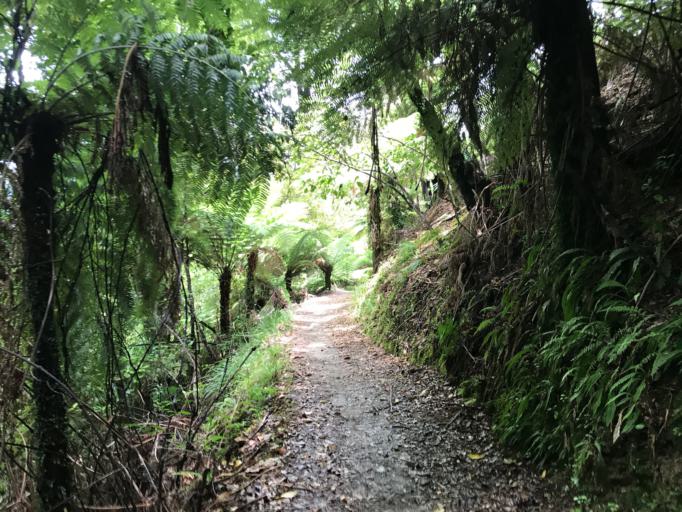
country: NZ
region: Marlborough
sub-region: Marlborough District
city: Picton
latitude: -41.2493
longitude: 173.9537
